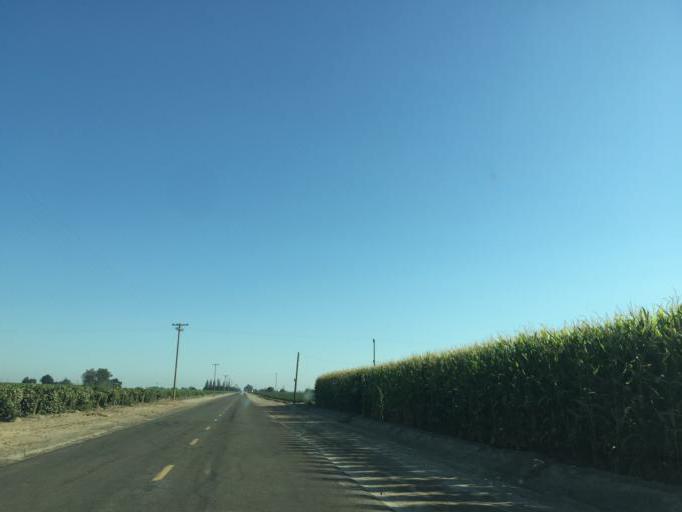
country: US
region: California
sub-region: Fresno County
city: Kingsburg
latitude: 36.4826
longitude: -119.5283
